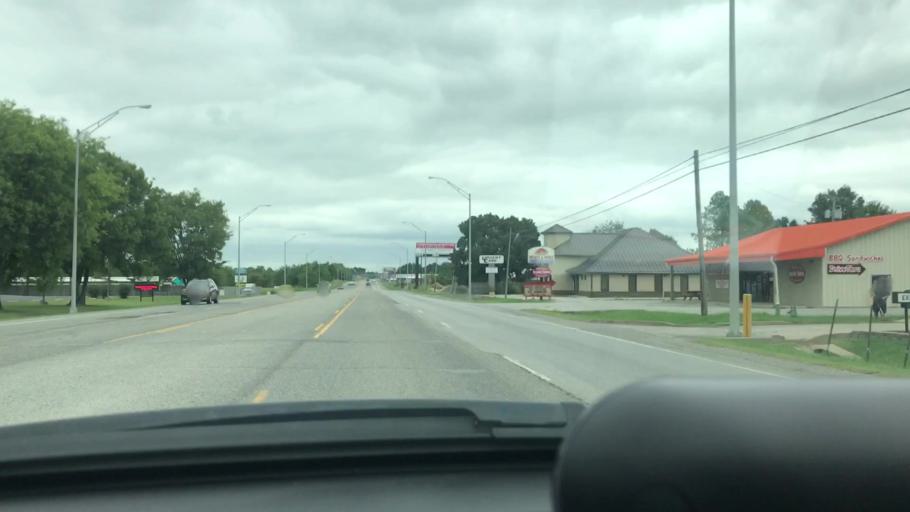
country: US
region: Oklahoma
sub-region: Wagoner County
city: Wagoner
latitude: 35.9468
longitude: -95.3952
